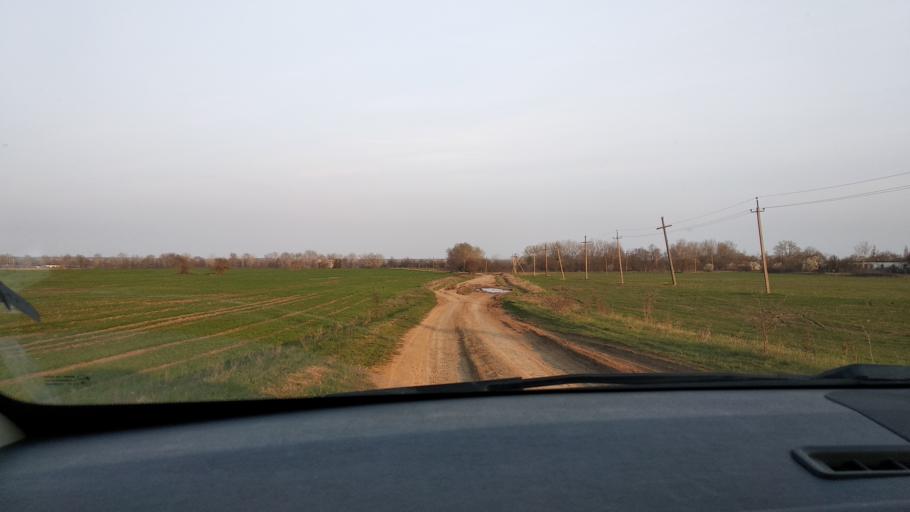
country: RU
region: Adygeya
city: Adygeysk
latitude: 44.8260
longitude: 39.2352
